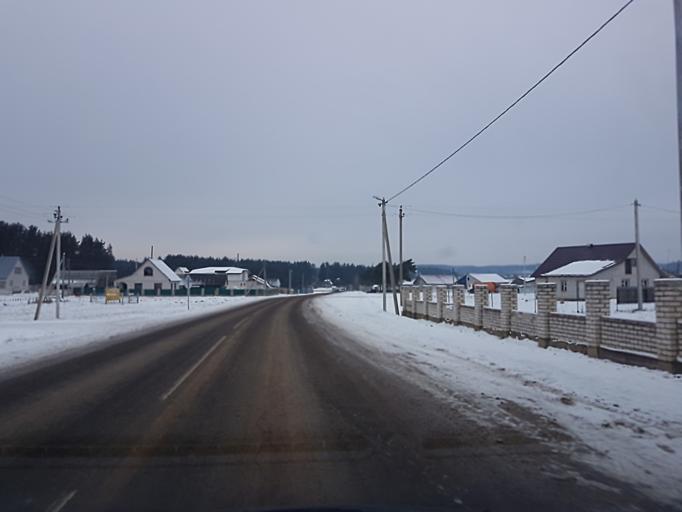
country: BY
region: Minsk
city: Rakaw
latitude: 53.9640
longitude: 27.0401
